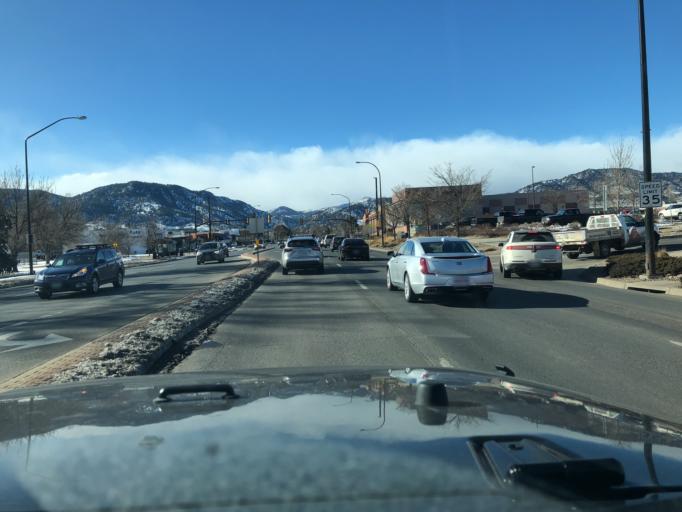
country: US
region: Colorado
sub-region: Boulder County
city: Boulder
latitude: 40.0147
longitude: -105.2545
